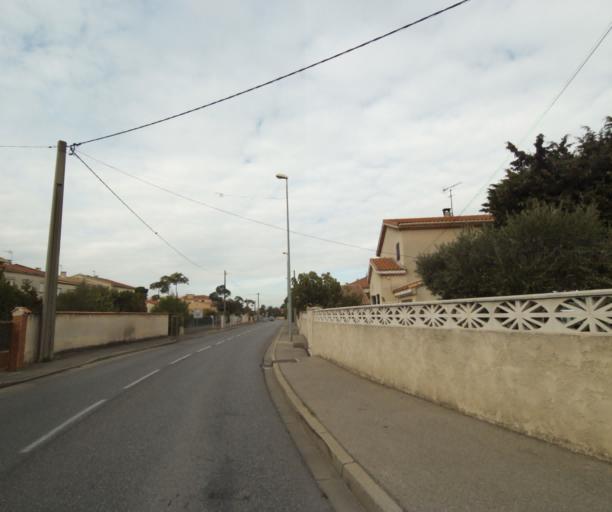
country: FR
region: Provence-Alpes-Cote d'Azur
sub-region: Departement des Bouches-du-Rhone
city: Saint-Victoret
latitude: 43.4190
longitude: 5.2438
